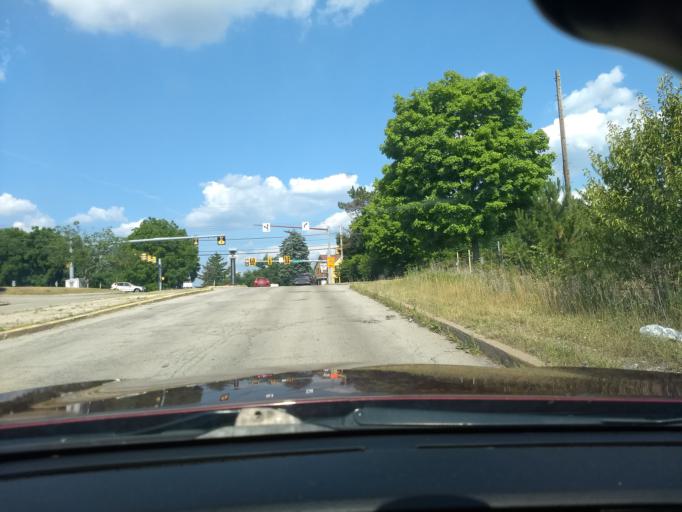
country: US
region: Pennsylvania
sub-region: Allegheny County
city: Pleasant Hills
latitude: 40.3402
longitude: -79.9392
